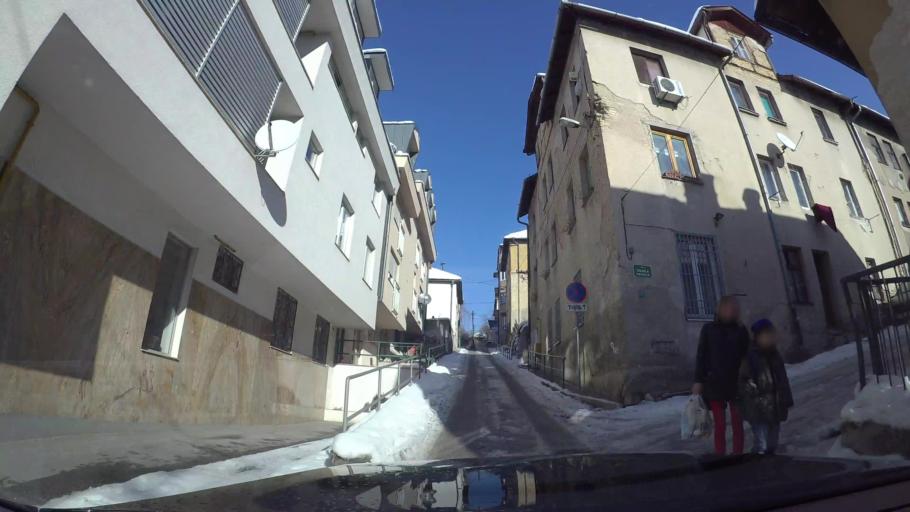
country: BA
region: Federation of Bosnia and Herzegovina
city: Kobilja Glava
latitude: 43.8625
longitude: 18.4209
